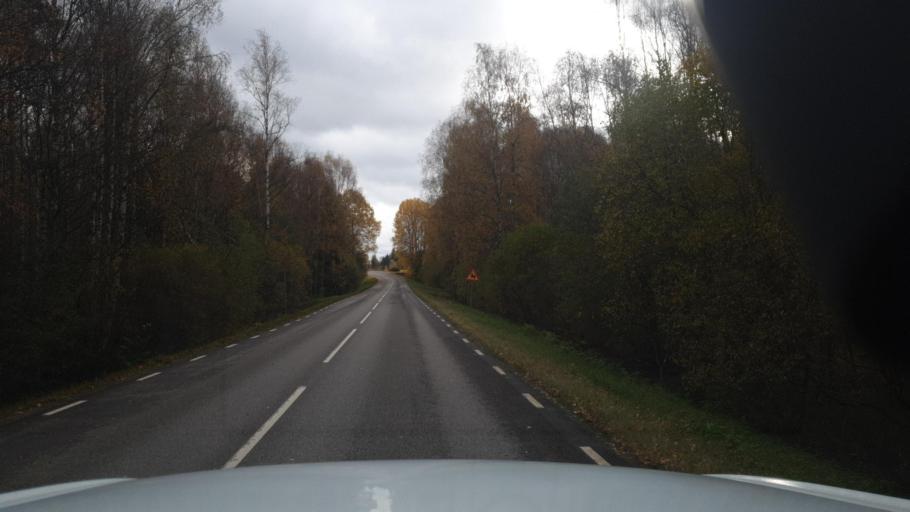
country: SE
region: Vaermland
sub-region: Sunne Kommun
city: Sunne
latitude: 59.8004
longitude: 13.0524
